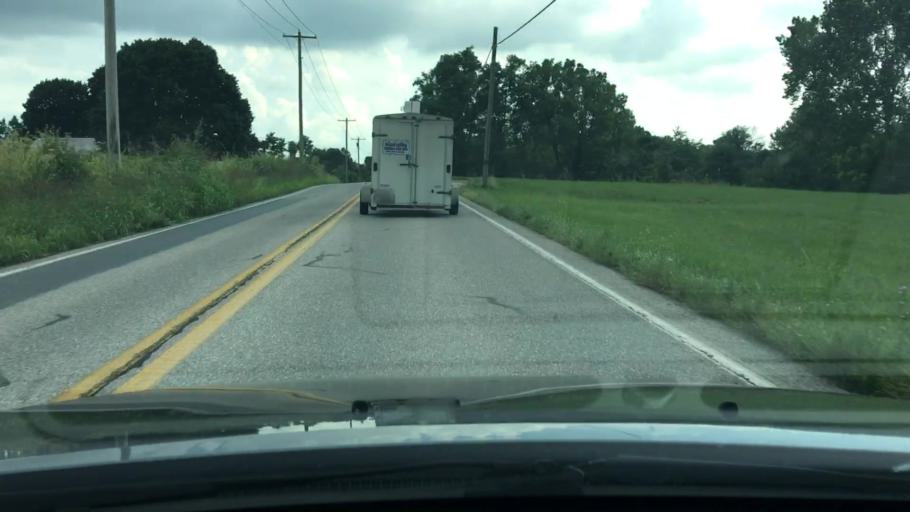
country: US
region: Pennsylvania
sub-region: Franklin County
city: Scotland
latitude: 39.9576
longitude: -77.5837
